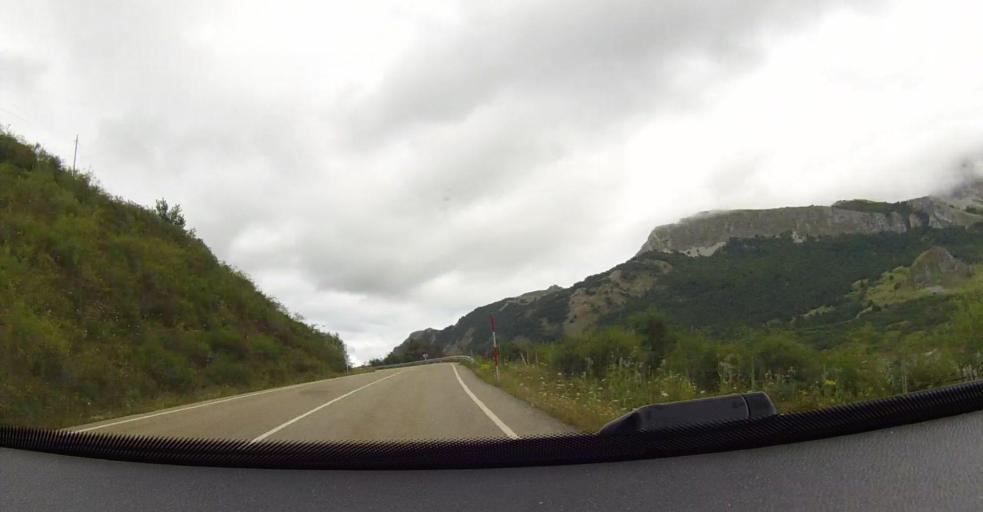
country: ES
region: Castille and Leon
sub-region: Provincia de Leon
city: Buron
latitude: 43.0221
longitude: -5.0419
